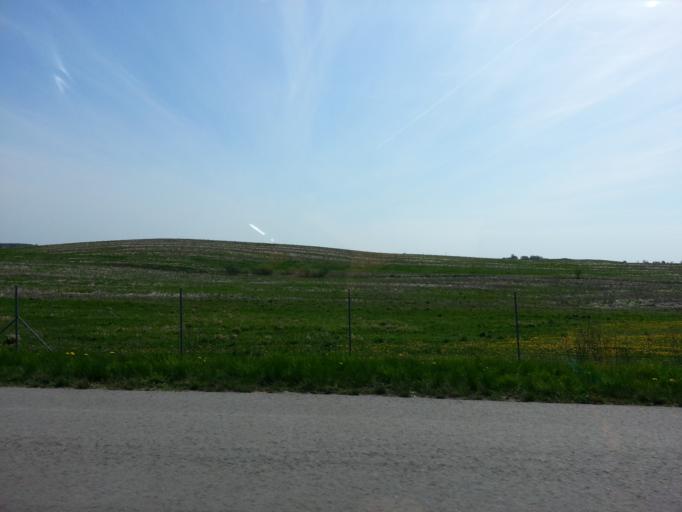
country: LT
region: Vilnius County
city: Ukmerge
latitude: 55.1961
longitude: 24.8138
